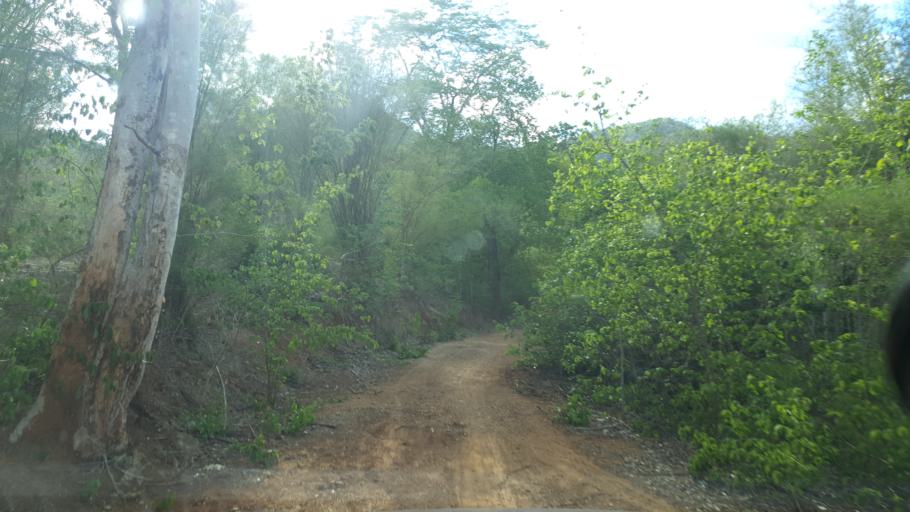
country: TH
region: Lampang
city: Sop Prap
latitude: 17.8524
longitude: 99.2840
